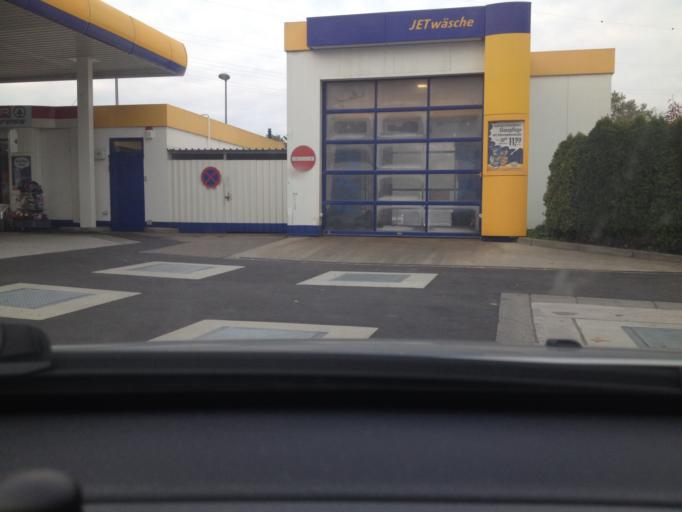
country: DE
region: Baden-Wuerttemberg
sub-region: Karlsruhe Region
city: Ispringen
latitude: 48.9047
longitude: 8.6548
